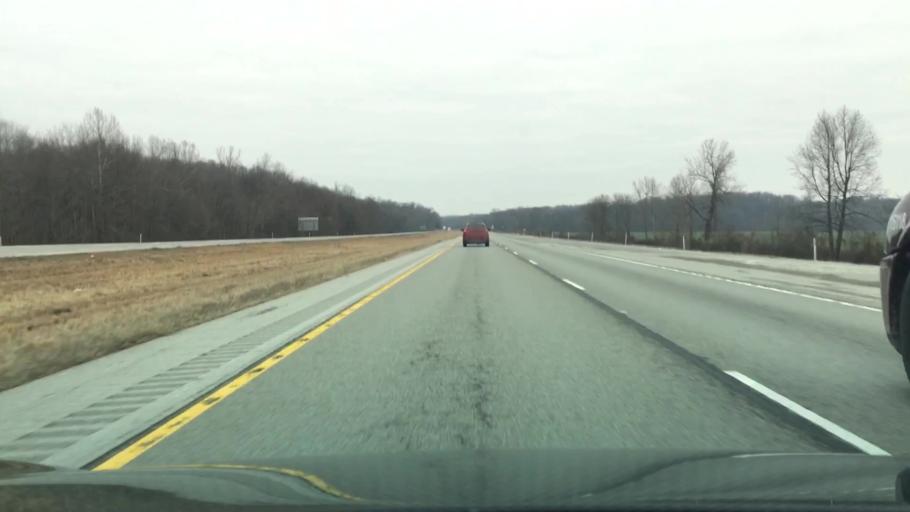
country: US
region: Illinois
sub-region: Massac County
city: Metropolis
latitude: 37.3041
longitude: -88.7542
